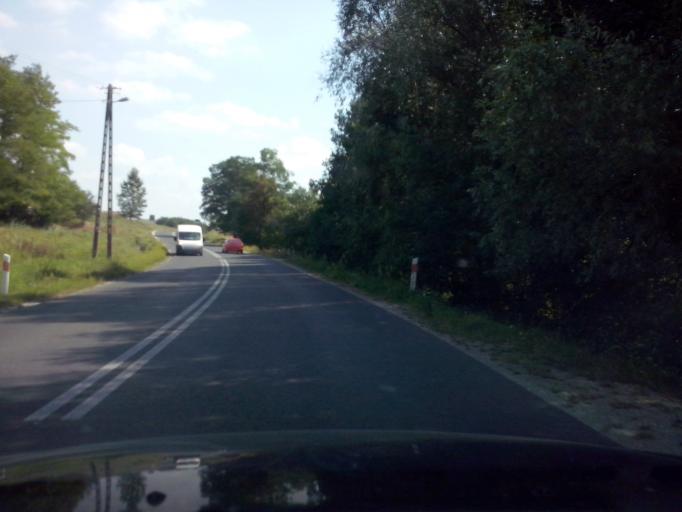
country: PL
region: Swietokrzyskie
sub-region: Powiat buski
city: Gnojno
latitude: 50.5910
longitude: 20.8882
